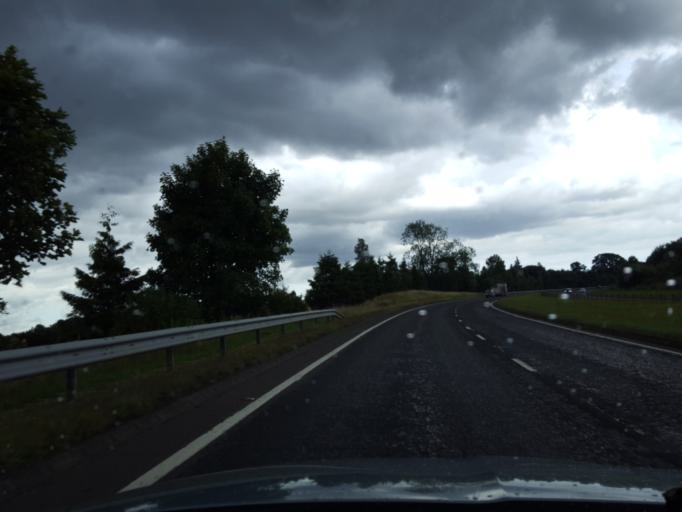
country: GB
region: Scotland
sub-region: Perth and Kinross
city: Bankfoot
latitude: 56.5366
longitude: -3.5252
